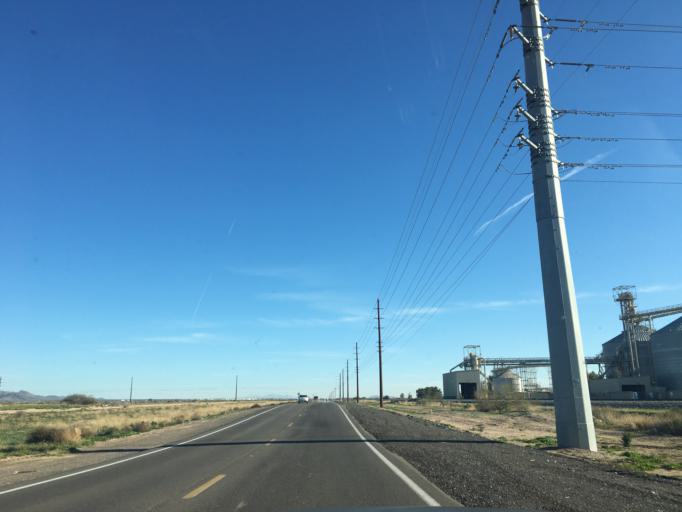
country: US
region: Arizona
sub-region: Pinal County
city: Maricopa
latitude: 33.0157
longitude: -111.9815
